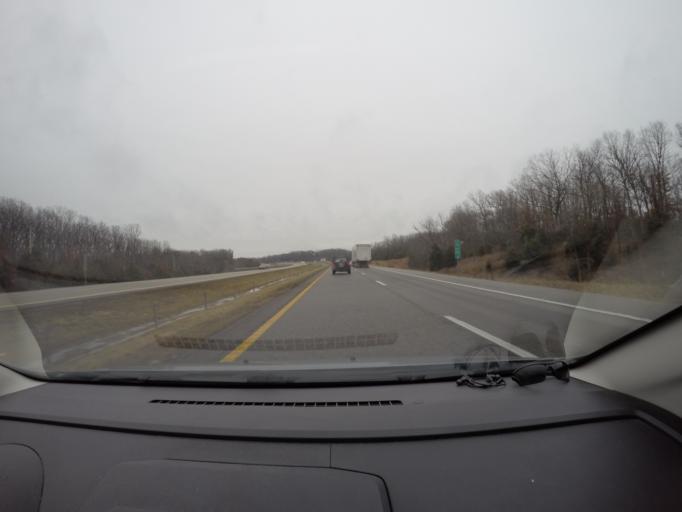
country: US
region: Missouri
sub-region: Montgomery County
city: Montgomery City
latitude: 38.8958
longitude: -91.6285
